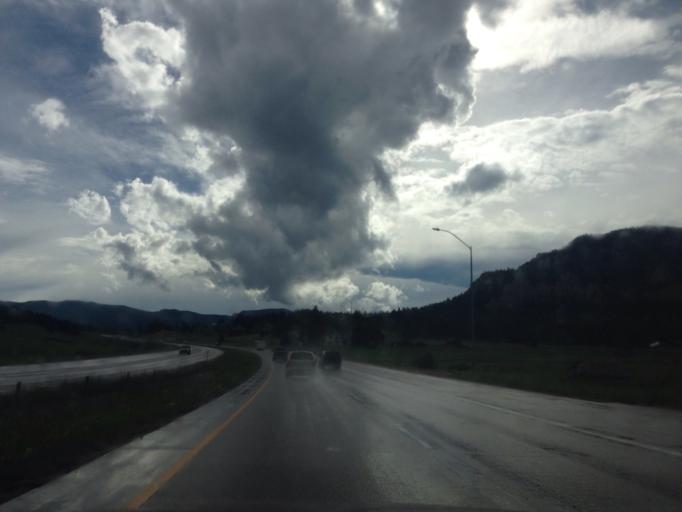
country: US
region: Colorado
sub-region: Jefferson County
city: Indian Hills
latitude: 39.5467
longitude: -105.2739
